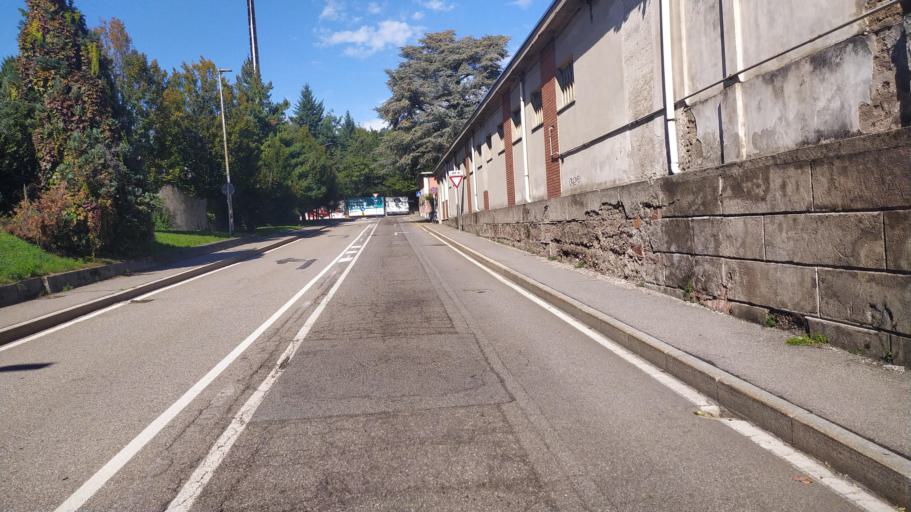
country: IT
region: Lombardy
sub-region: Provincia di Varese
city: Varese
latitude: 45.8147
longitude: 8.8091
